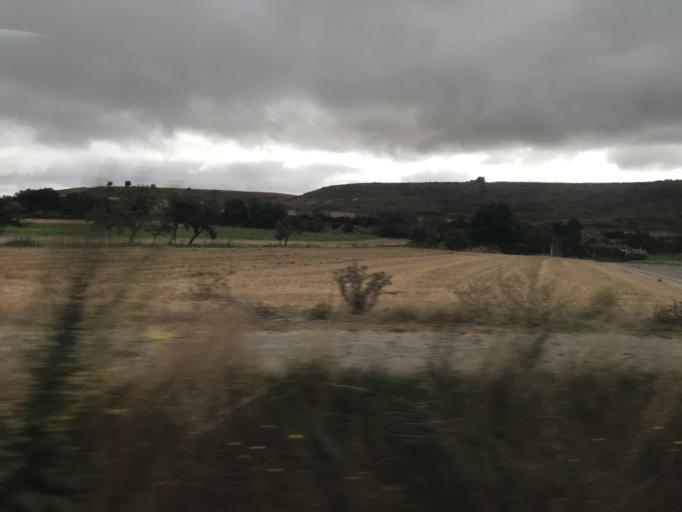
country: ES
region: Castille and Leon
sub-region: Provincia de Burgos
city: Miranda de Ebro
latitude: 42.6698
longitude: -2.9769
